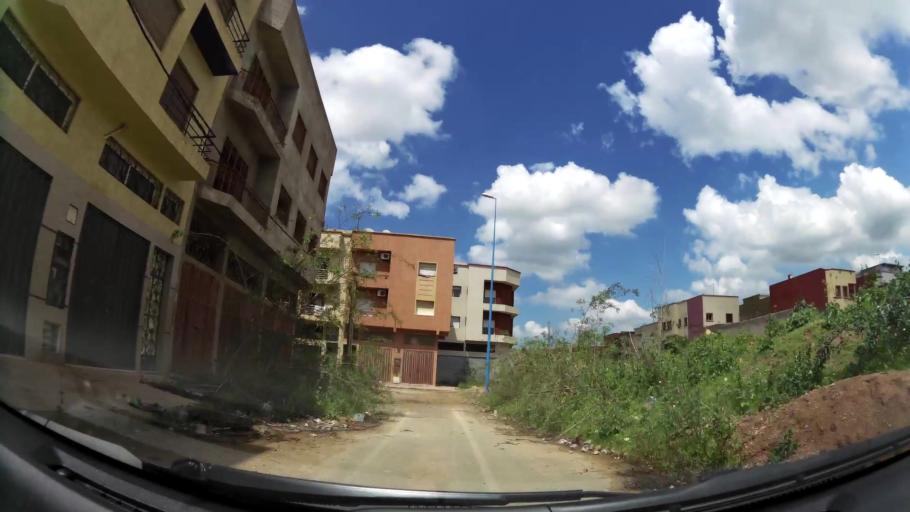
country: MA
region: Grand Casablanca
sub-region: Mediouna
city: Mediouna
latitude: 33.3861
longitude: -7.5458
